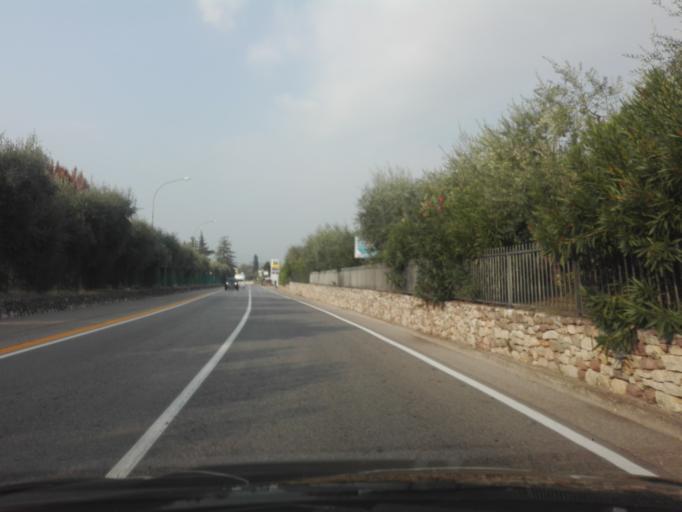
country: IT
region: Veneto
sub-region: Provincia di Verona
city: Lazise
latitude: 45.4950
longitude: 10.7387
